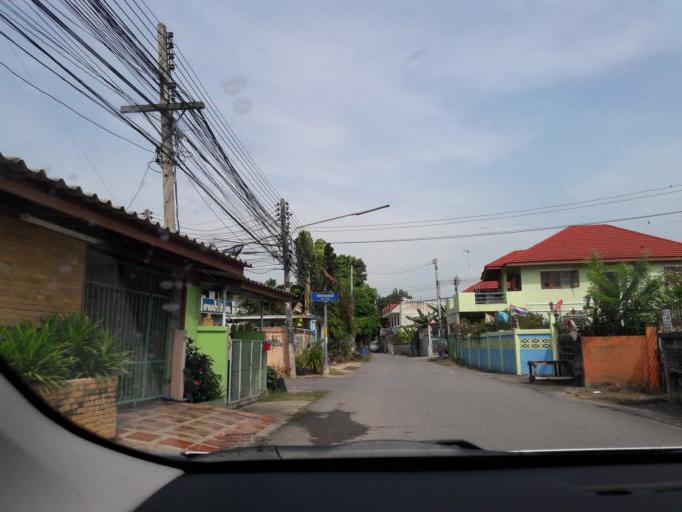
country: TH
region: Ang Thong
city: Ang Thong
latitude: 14.5829
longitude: 100.4631
